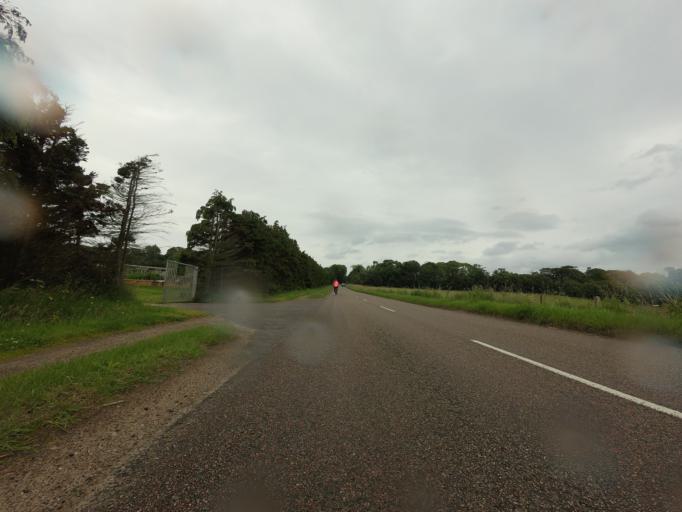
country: GB
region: Scotland
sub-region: Moray
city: Cullen
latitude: 57.6817
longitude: -2.8139
